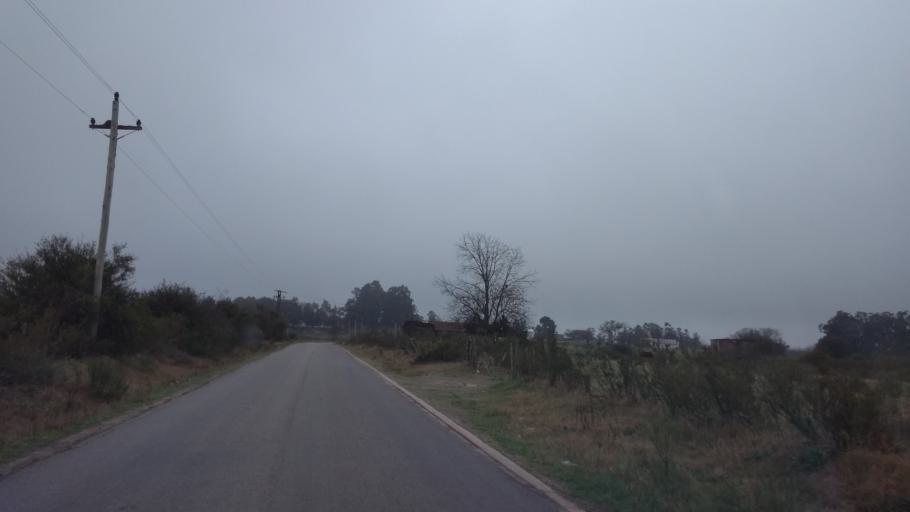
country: UY
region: Florida
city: Florida
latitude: -34.0833
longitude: -56.2052
